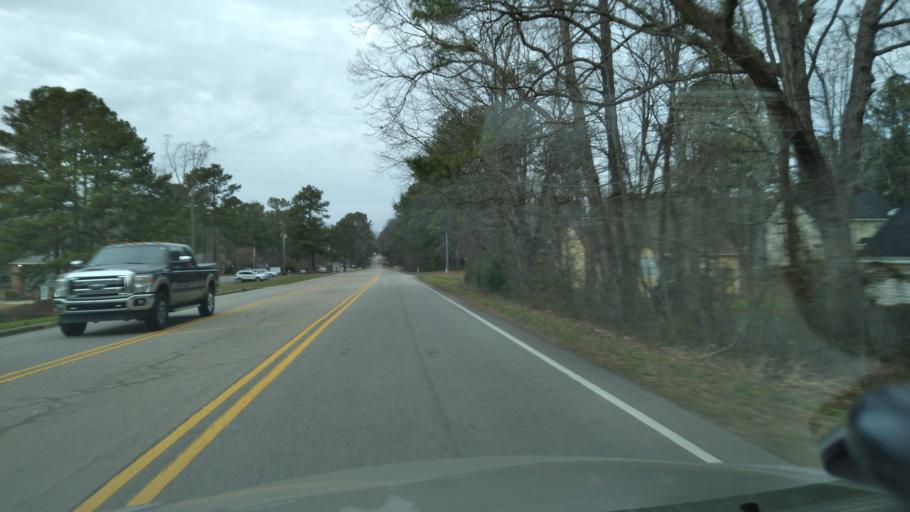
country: US
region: North Carolina
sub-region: Wake County
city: Garner
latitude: 35.6918
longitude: -78.6064
